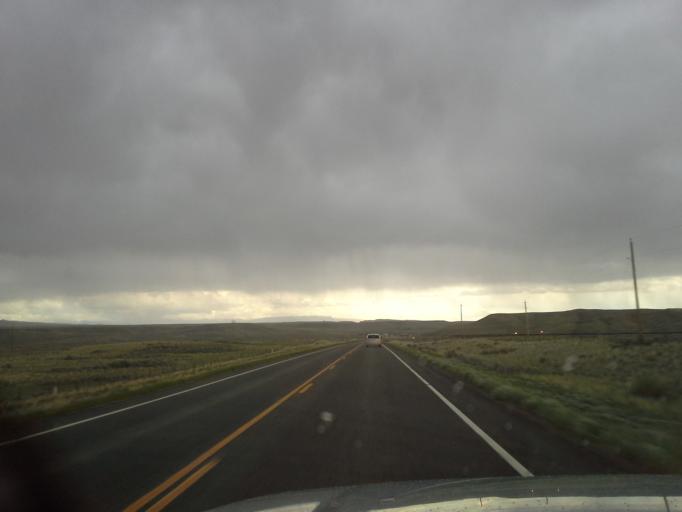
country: US
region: Wyoming
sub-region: Park County
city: Powell
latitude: 45.0692
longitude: -108.6786
